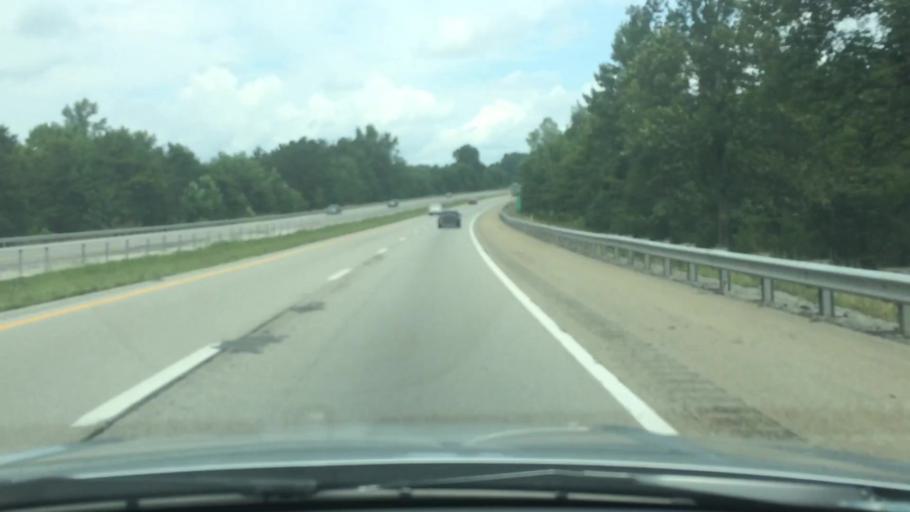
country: US
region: Kentucky
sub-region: Whitley County
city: Corbin
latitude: 36.8838
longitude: -84.1505
